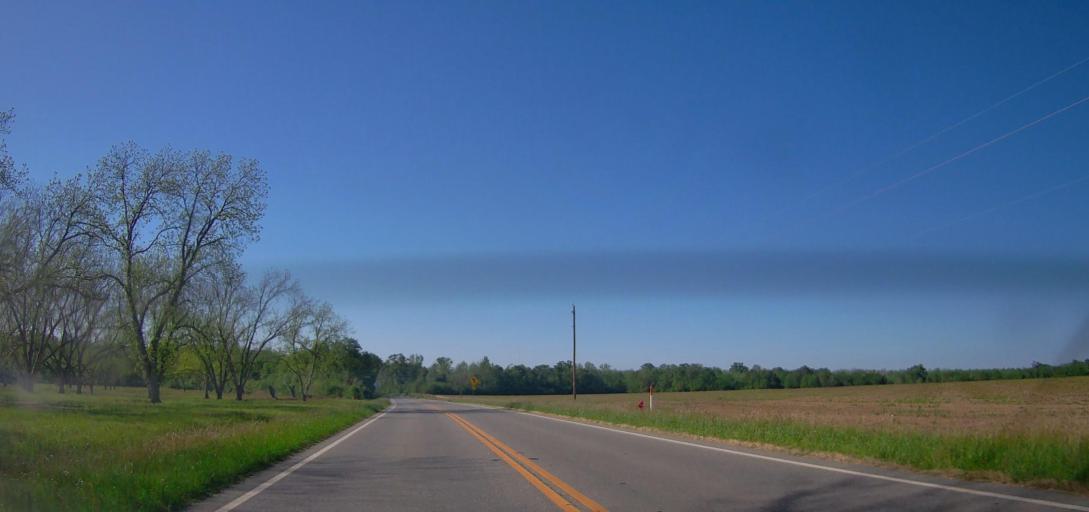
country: US
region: Georgia
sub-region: Wilcox County
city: Rochelle
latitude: 31.9426
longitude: -83.4429
